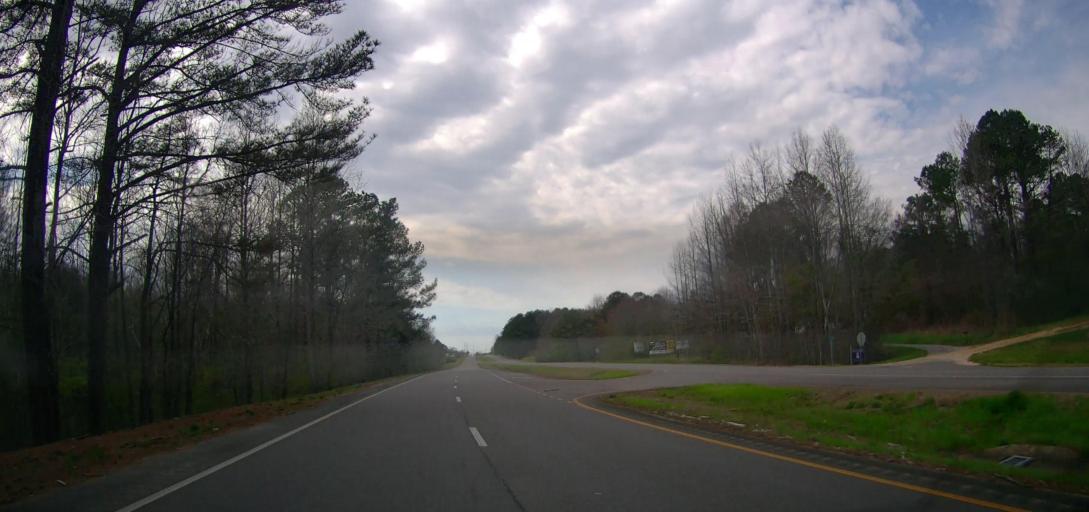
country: US
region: Alabama
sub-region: Marion County
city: Winfield
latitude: 33.9285
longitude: -87.7605
